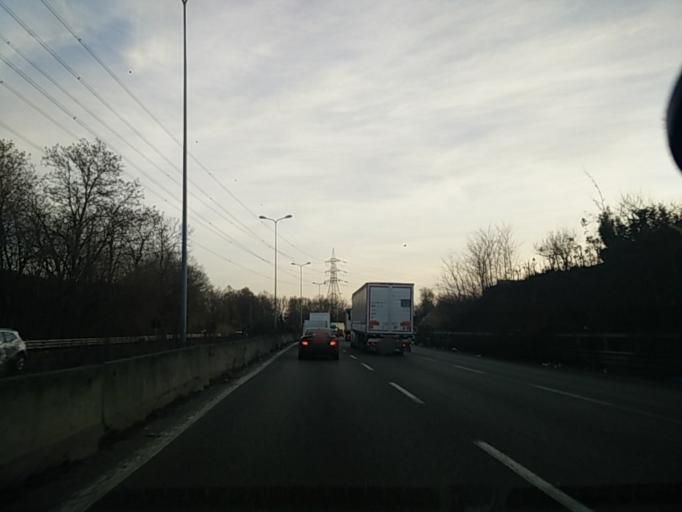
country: IT
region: Lombardy
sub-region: Provincia di Monza e Brianza
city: Varedo
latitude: 45.5996
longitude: 9.1710
